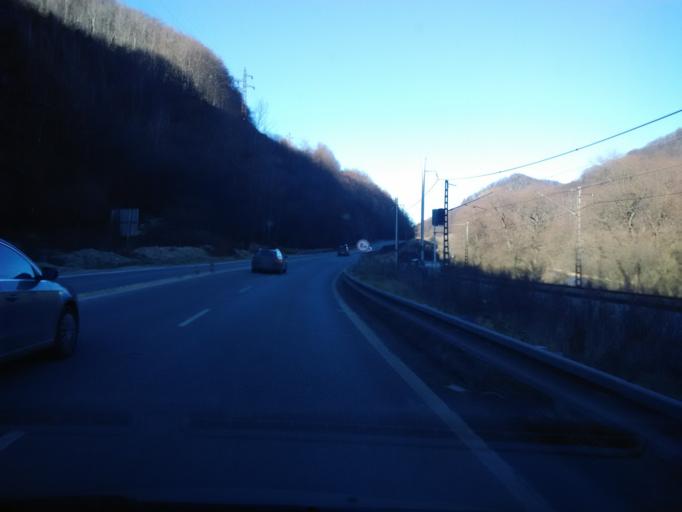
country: SK
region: Zilinsky
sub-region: Okres Zilina
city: Vrutky
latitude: 49.1440
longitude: 18.8903
